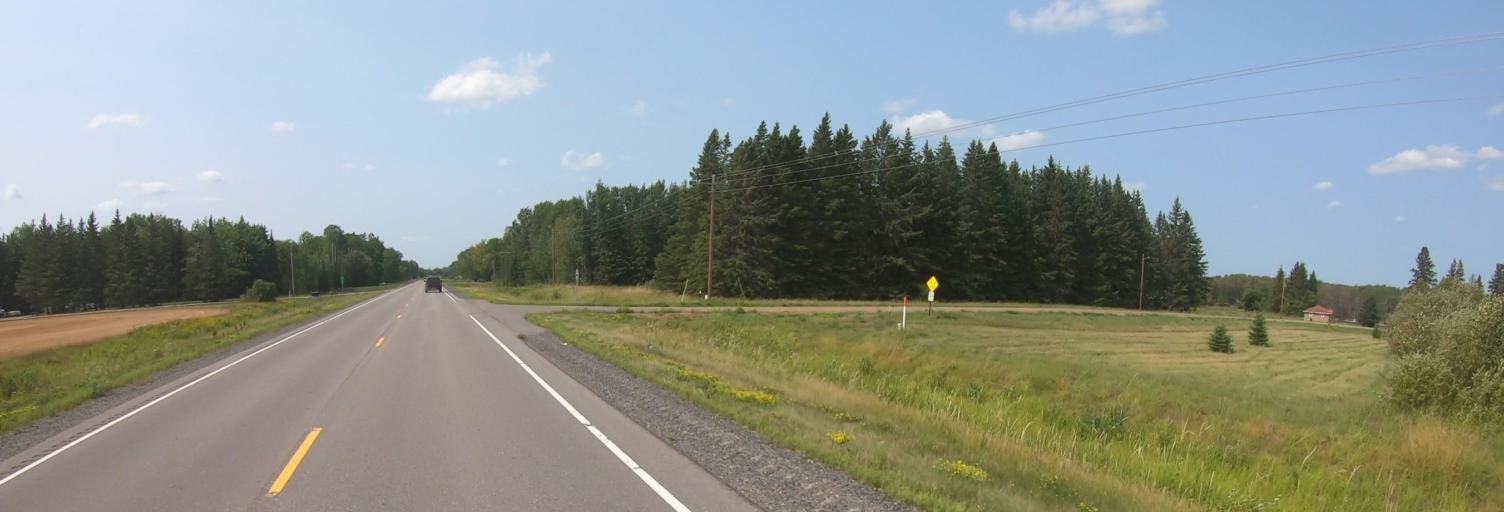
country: US
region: Minnesota
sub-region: Lake of the Woods County
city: Baudette
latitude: 48.6978
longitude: -94.5242
